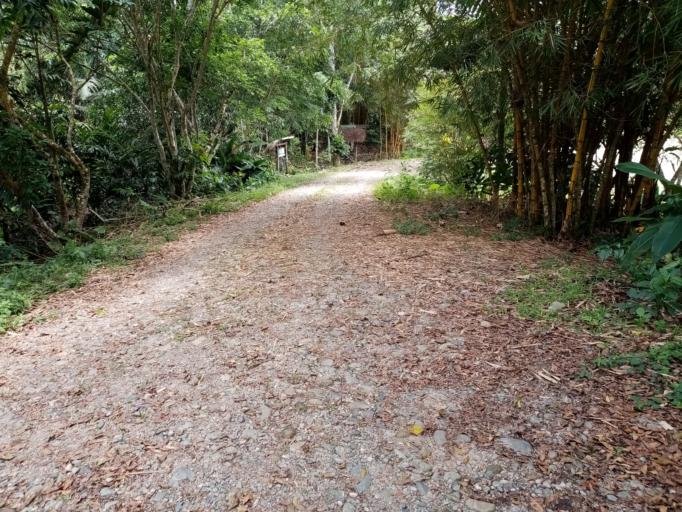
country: EC
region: Napo
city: Tena
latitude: -0.9729
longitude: -77.8003
